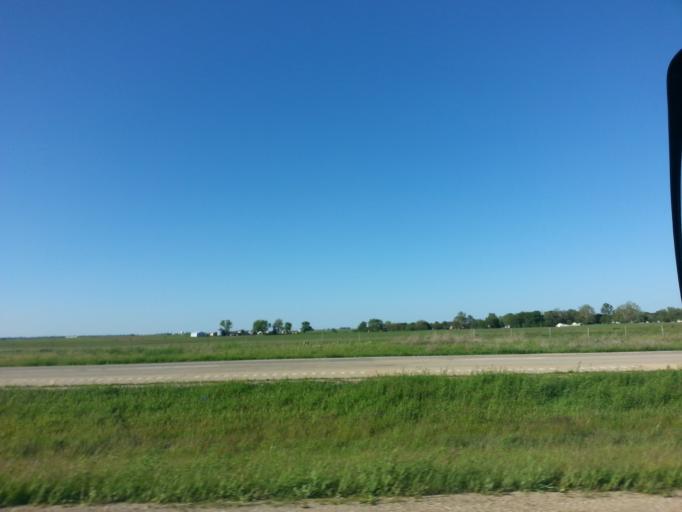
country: US
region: Illinois
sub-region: Woodford County
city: El Paso
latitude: 40.6736
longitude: -89.0201
